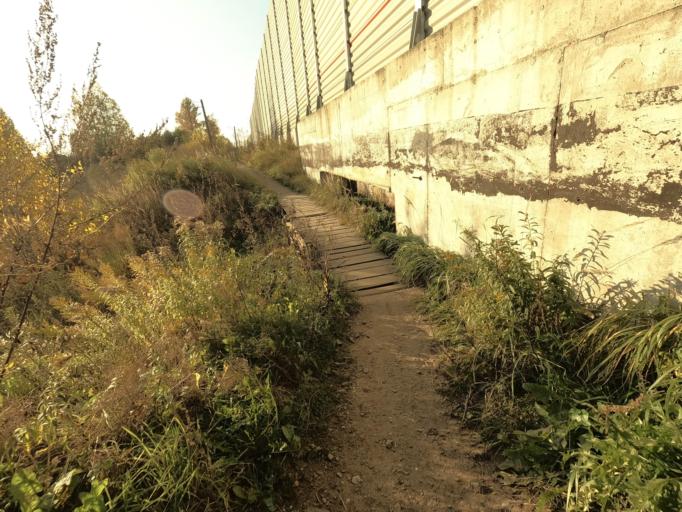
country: RU
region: Leningrad
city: Mga
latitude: 59.7564
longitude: 31.0520
